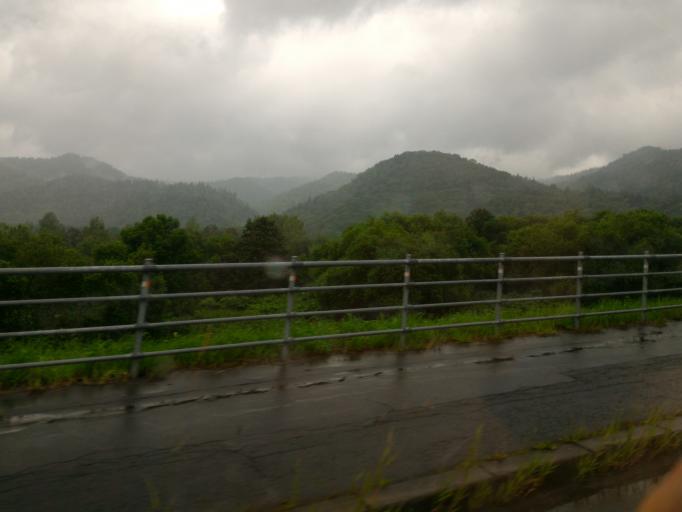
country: JP
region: Hokkaido
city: Nayoro
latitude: 44.7328
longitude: 142.1946
